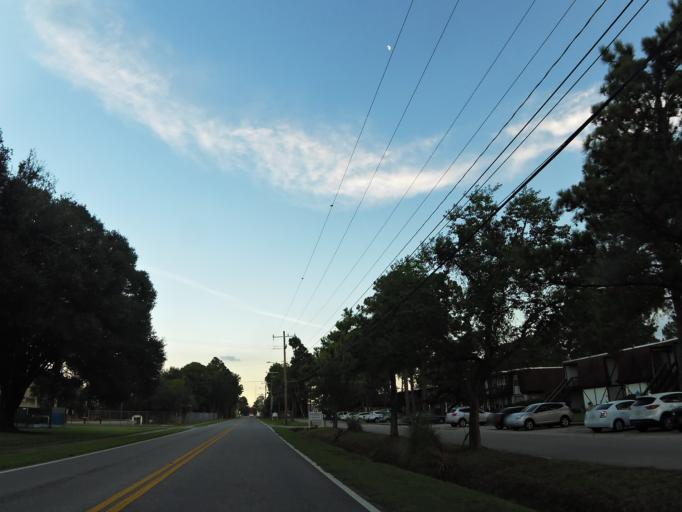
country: US
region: Florida
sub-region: Duval County
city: Jacksonville
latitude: 30.2710
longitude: -81.6168
